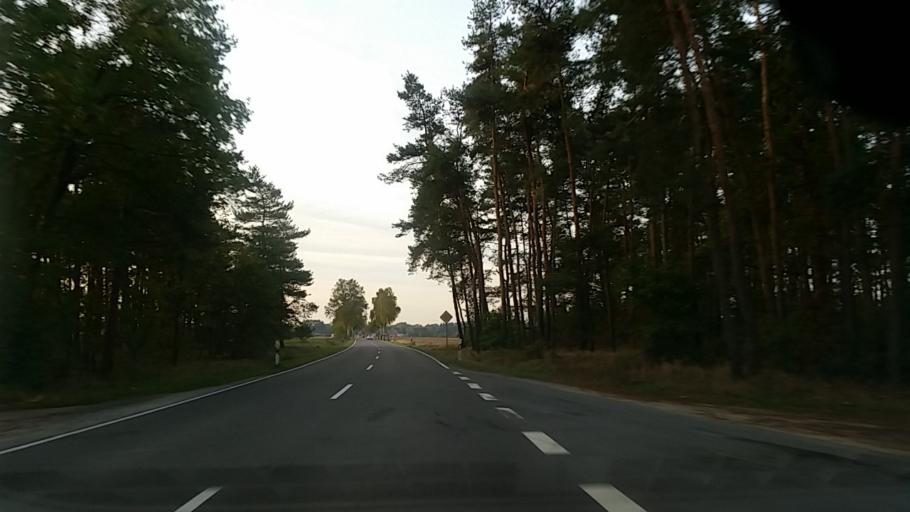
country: DE
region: Lower Saxony
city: Barwedel
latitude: 52.5798
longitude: 10.7872
